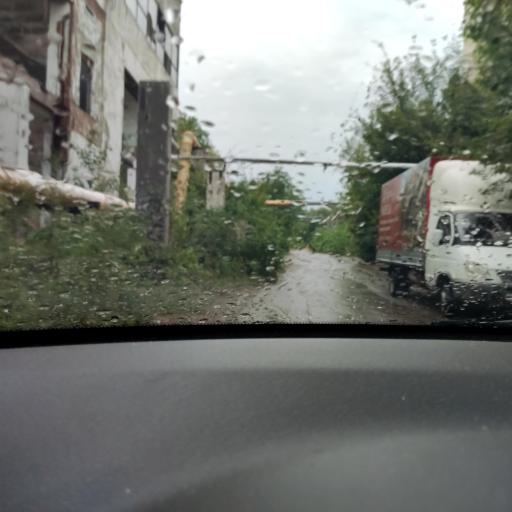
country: RU
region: Samara
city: Samara
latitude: 53.2216
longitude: 50.1479
